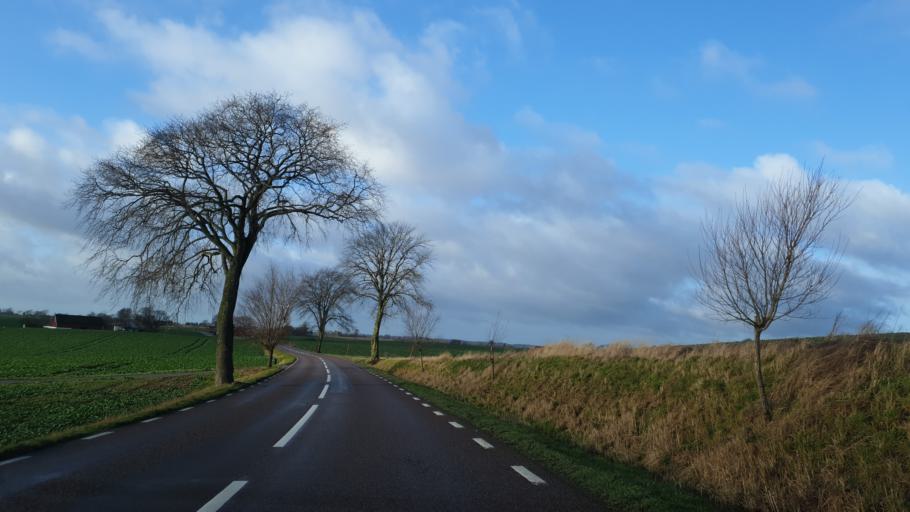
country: SE
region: Skane
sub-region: Skurups Kommun
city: Skurup
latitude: 55.4236
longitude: 13.4424
